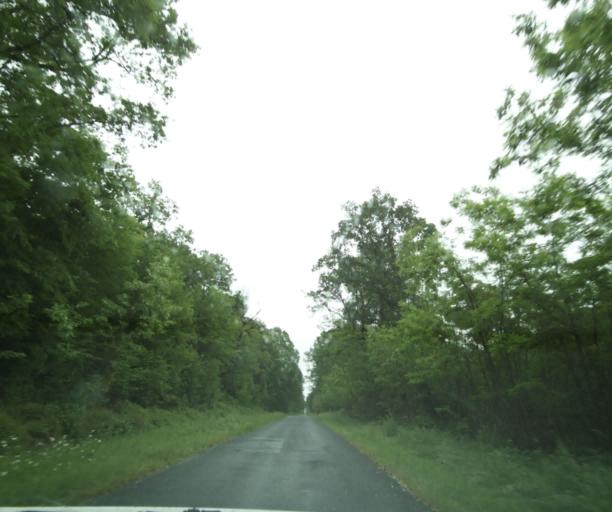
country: FR
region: Bourgogne
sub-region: Departement de Saone-et-Loire
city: Palinges
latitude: 46.5248
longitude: 4.2313
